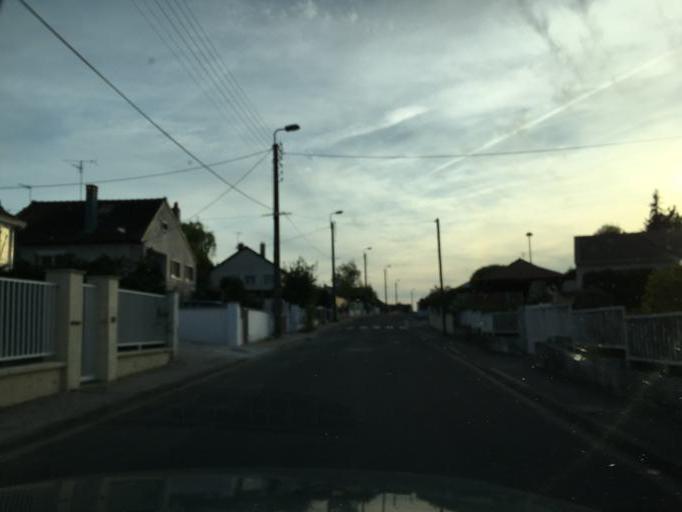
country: FR
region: Centre
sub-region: Departement du Loiret
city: Saran
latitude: 47.9472
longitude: 1.8714
